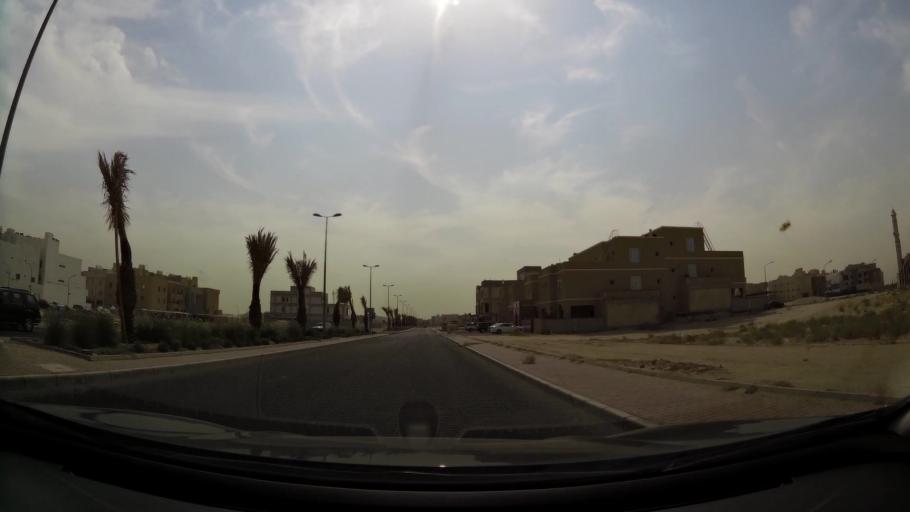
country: KW
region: Al Farwaniyah
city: Janub as Surrah
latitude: 29.2948
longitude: 47.9973
